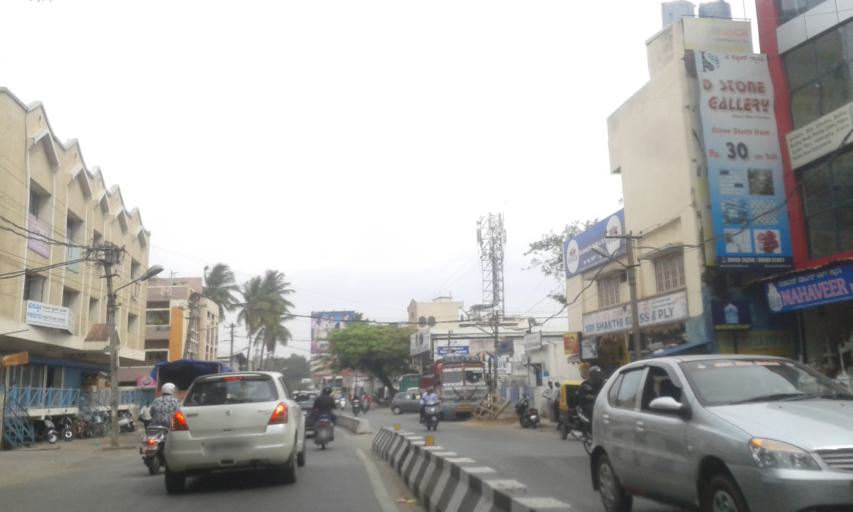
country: IN
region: Karnataka
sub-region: Bangalore Urban
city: Bangalore
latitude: 12.9485
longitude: 77.6027
